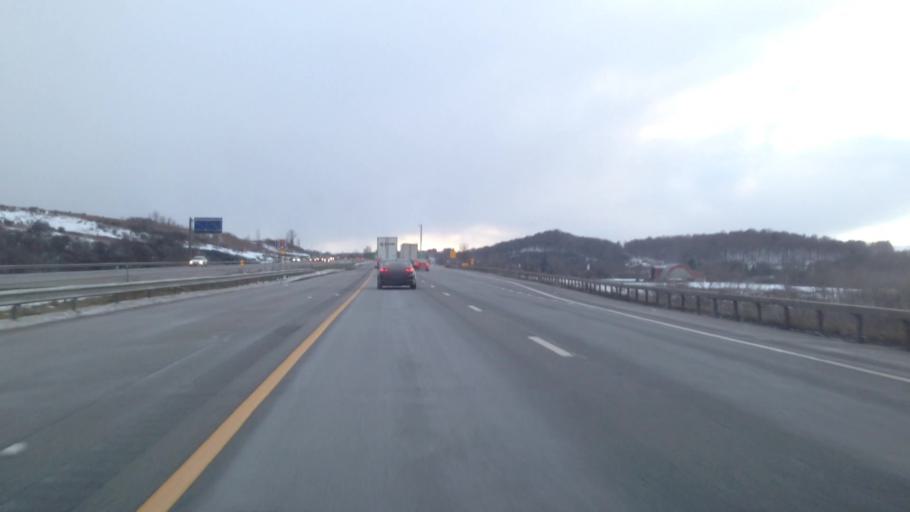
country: US
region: New York
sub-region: Herkimer County
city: Little Falls
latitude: 43.0170
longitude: -74.8116
